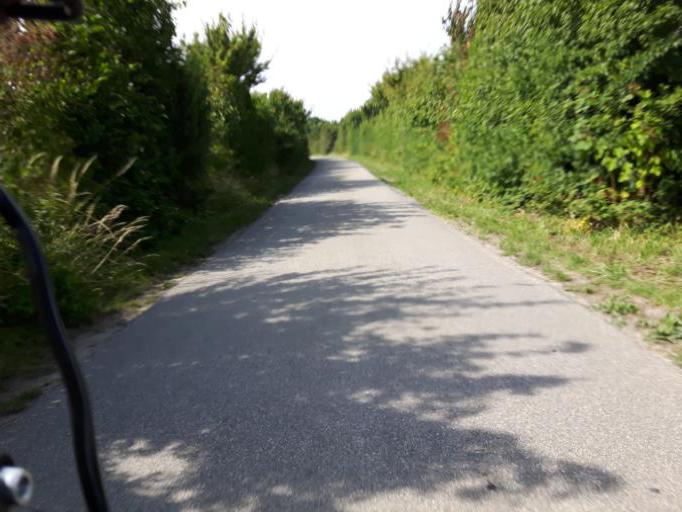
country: NL
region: Zeeland
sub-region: Gemeente Middelburg
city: Middelburg
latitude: 51.4687
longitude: 3.6396
